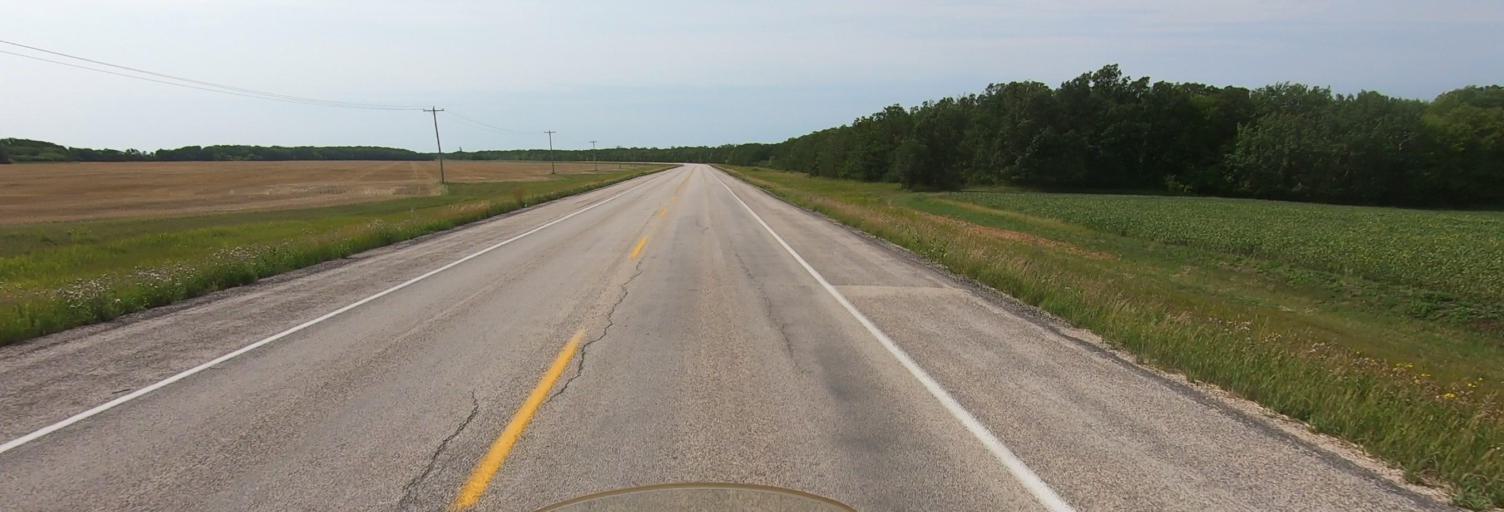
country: CA
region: Manitoba
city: Niverville
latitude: 49.6027
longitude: -97.1317
